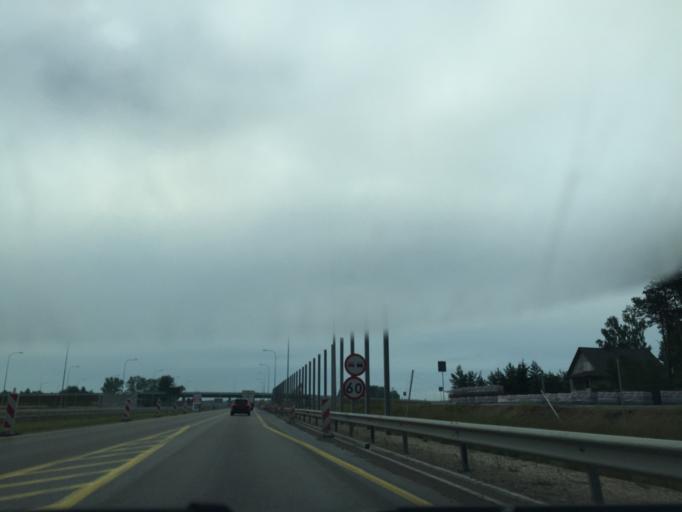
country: PL
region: Podlasie
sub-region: Powiat zambrowski
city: Szumowo
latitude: 52.9081
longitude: 22.0946
